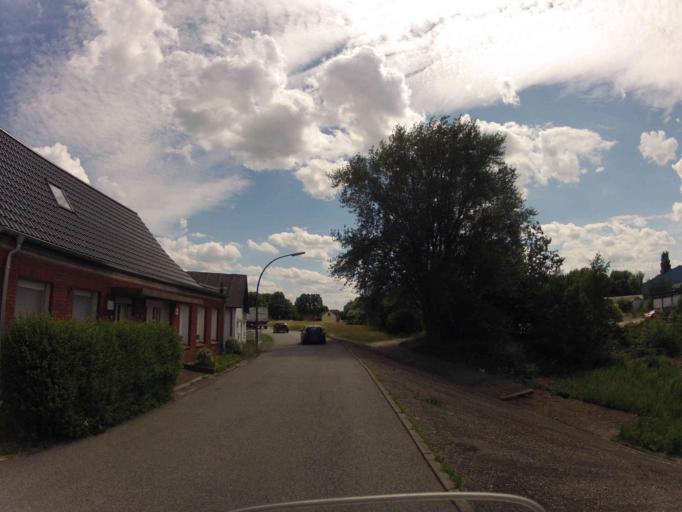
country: DE
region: Hamburg
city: Rothenburgsort
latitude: 53.5116
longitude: 10.0747
